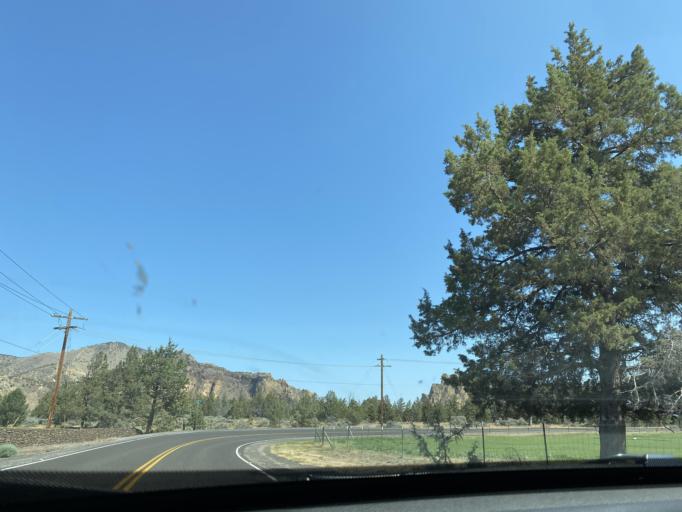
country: US
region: Oregon
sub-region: Deschutes County
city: Terrebonne
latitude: 44.3705
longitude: -121.1646
